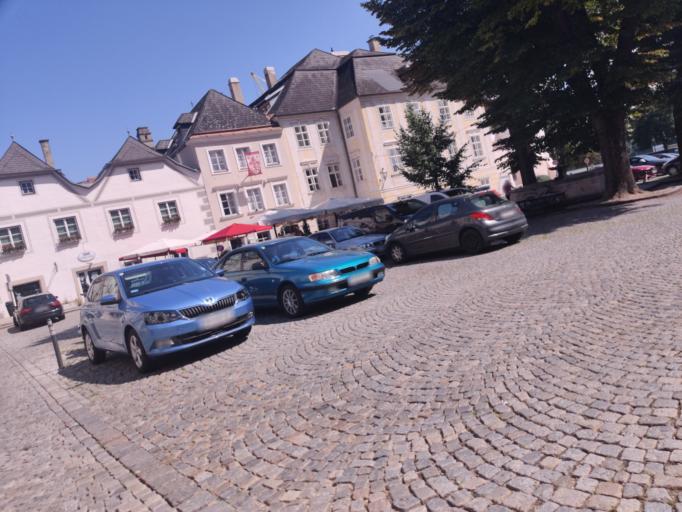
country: AT
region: Lower Austria
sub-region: Politischer Bezirk Krems
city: Weinzierl bei Krems
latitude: 48.4015
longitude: 15.5800
